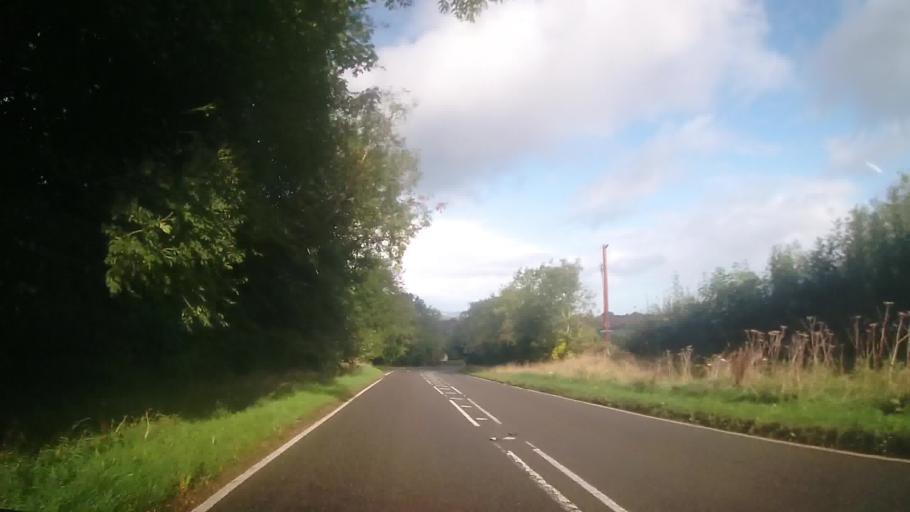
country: GB
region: England
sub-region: Oxfordshire
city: Chipping Norton
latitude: 51.9621
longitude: -1.6185
